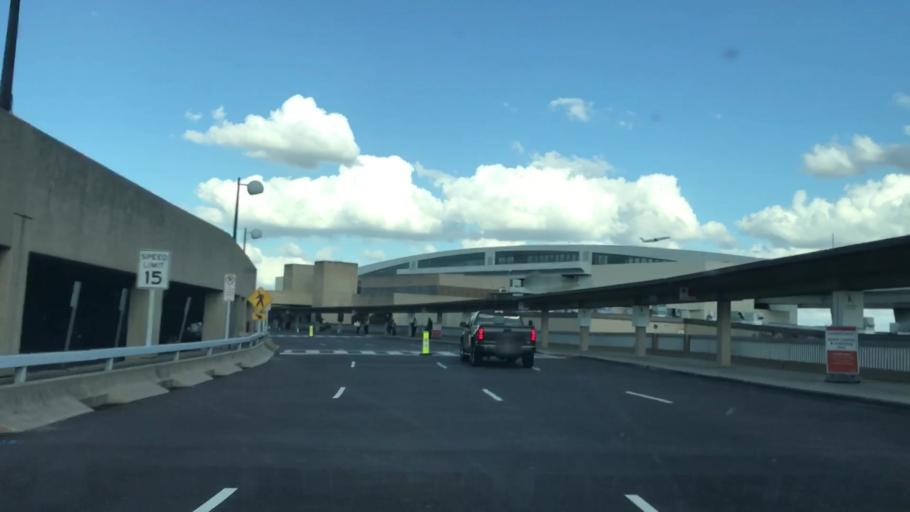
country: US
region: Texas
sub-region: Tarrant County
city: Grapevine
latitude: 32.8956
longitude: -97.0385
